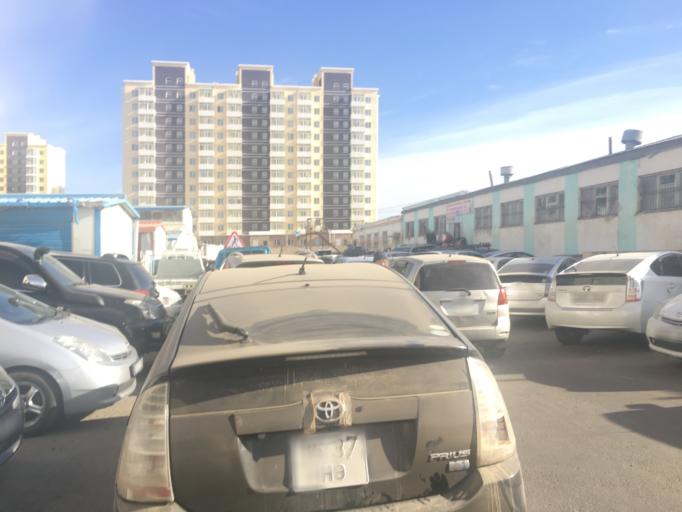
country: MN
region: Ulaanbaatar
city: Ulaanbaatar
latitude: 47.9093
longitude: 106.8368
